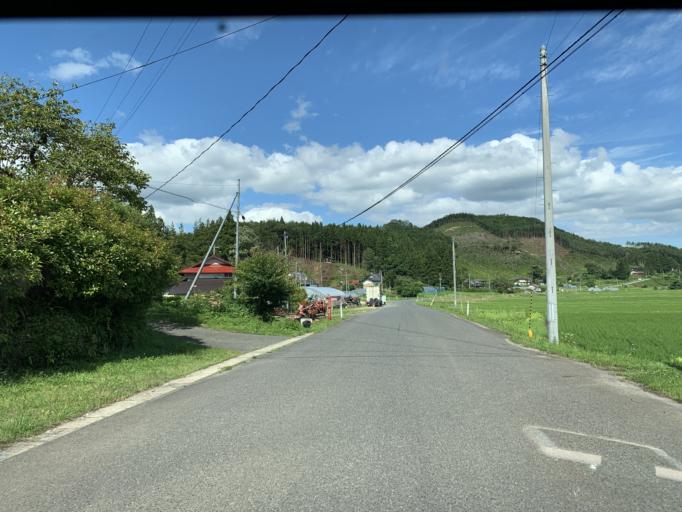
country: JP
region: Iwate
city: Ichinoseki
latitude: 38.9635
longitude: 140.9477
